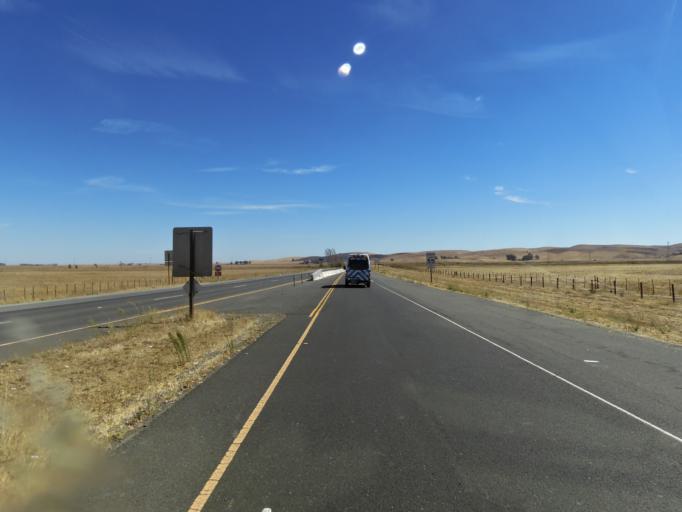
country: US
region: California
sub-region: Solano County
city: Suisun
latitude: 38.2382
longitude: -121.9873
